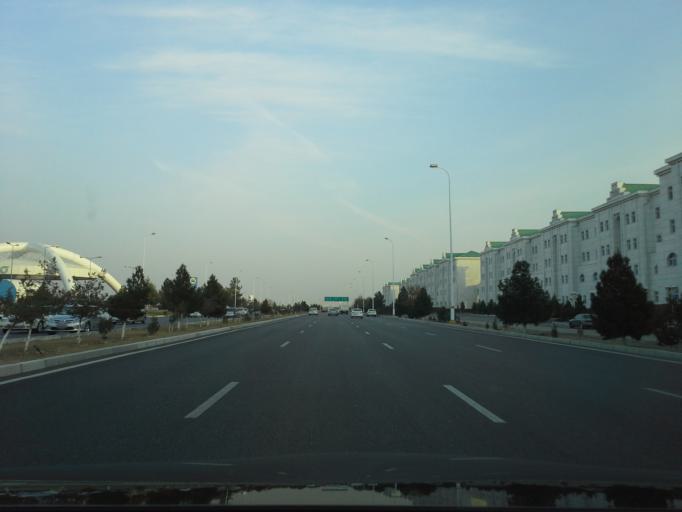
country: TM
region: Ahal
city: Ashgabat
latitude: 37.9889
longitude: 58.3220
